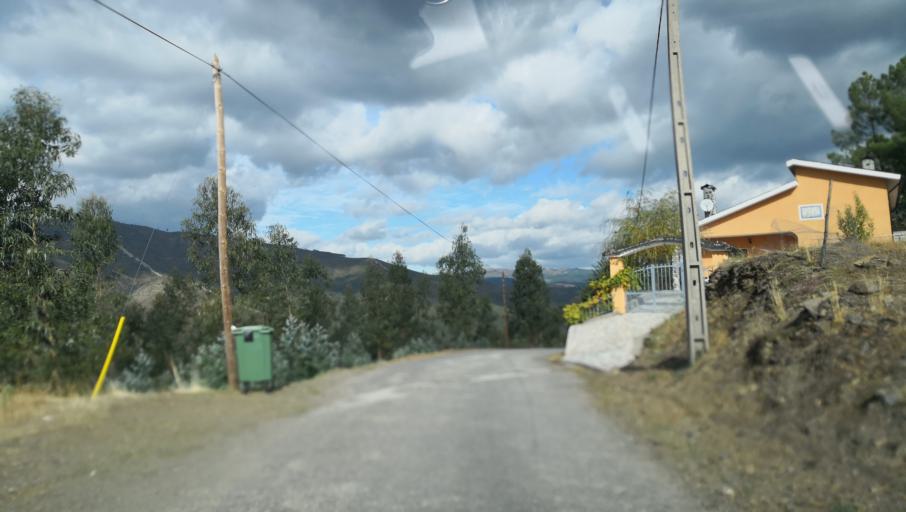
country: PT
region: Vila Real
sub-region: Mondim de Basto
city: Mondim de Basto
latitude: 41.3532
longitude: -7.8921
